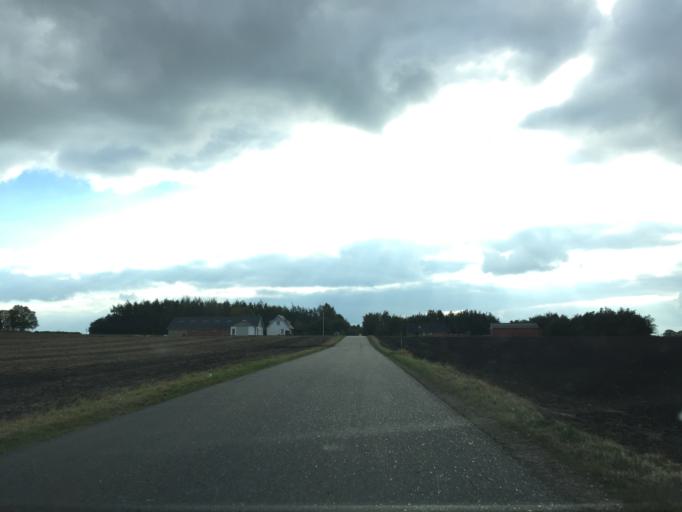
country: DK
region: Central Jutland
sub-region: Favrskov Kommune
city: Ulstrup
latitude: 56.2987
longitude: 9.7707
